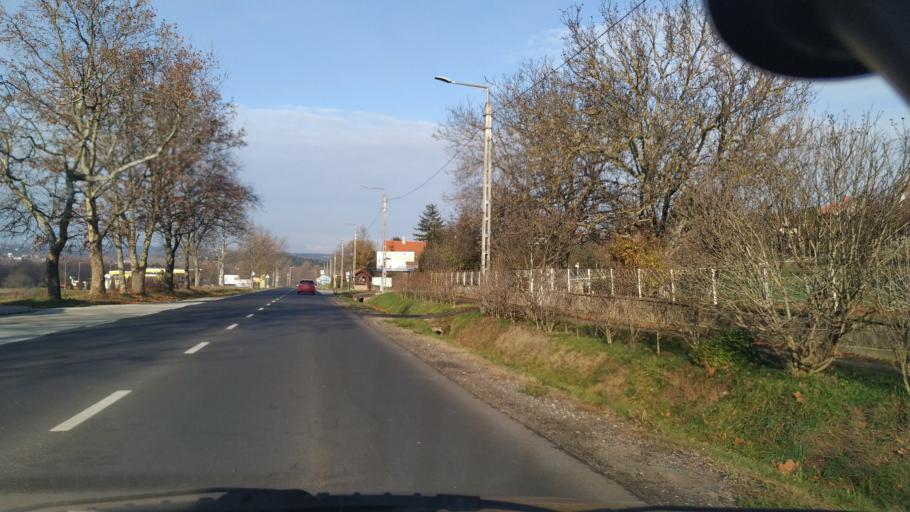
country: HU
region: Zala
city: Cserszegtomaj
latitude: 46.7856
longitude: 17.2162
